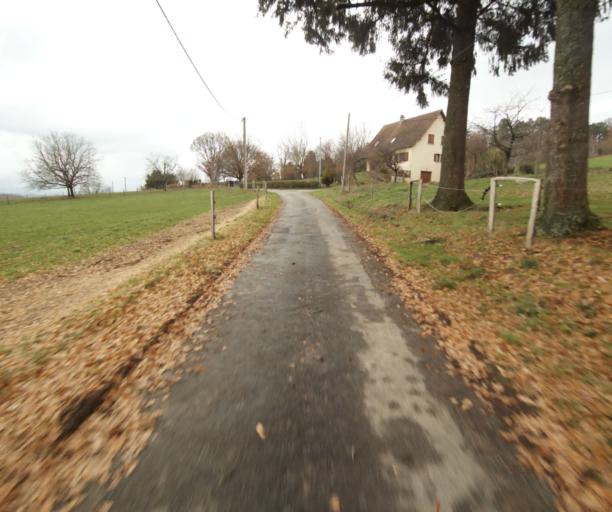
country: FR
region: Limousin
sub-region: Departement de la Correze
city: Saint-Mexant
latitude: 45.2813
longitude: 1.6230
